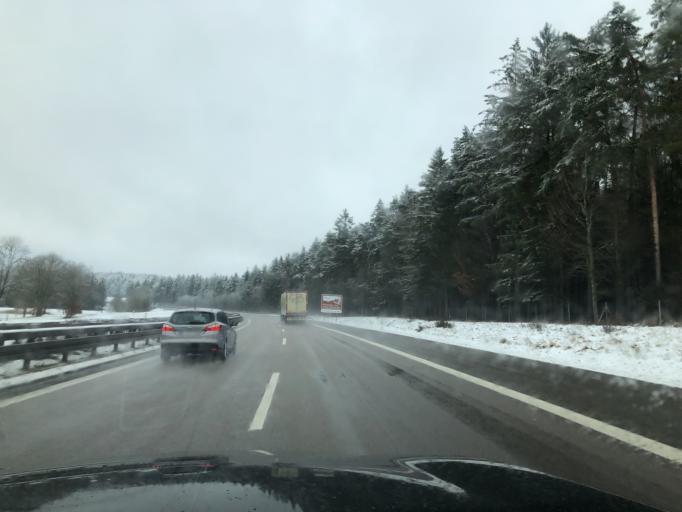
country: DE
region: Bavaria
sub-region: Regierungsbezirk Mittelfranken
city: Alfeld
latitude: 49.4128
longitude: 11.5677
